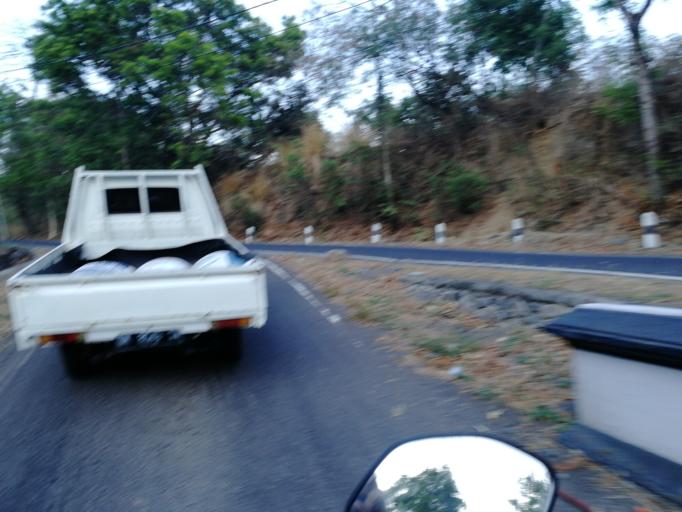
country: ID
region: Bali
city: Biaslantang Kaler
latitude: -8.3384
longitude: 115.6214
